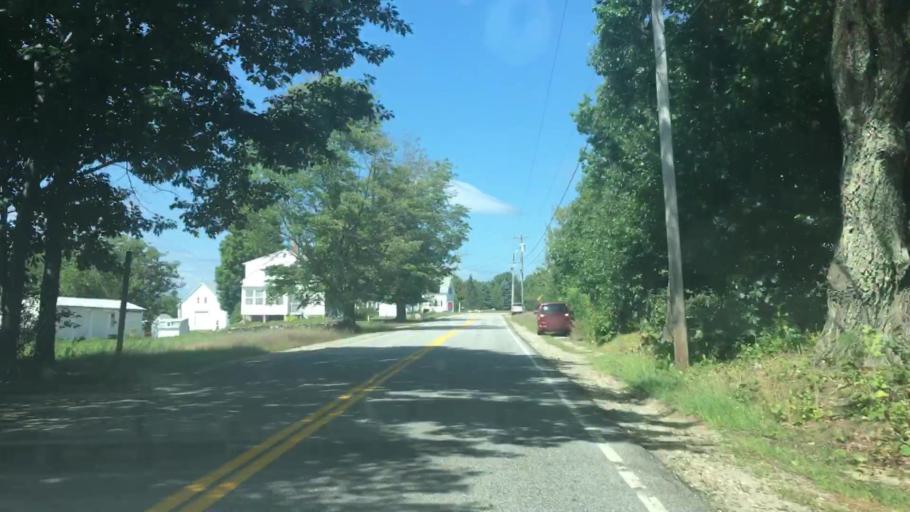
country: US
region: Maine
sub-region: Androscoggin County
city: Lisbon
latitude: 44.0533
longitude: -70.1157
